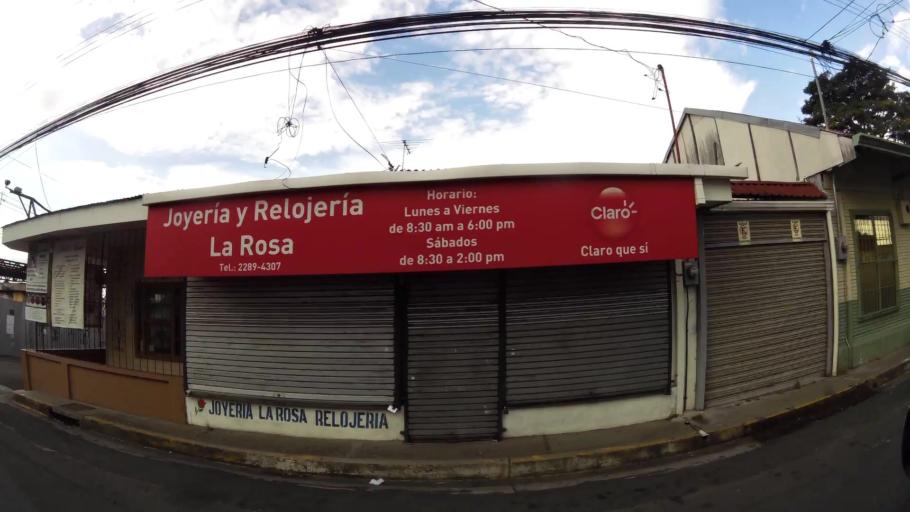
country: CR
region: San Jose
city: Escazu
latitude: 9.9202
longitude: -84.1380
